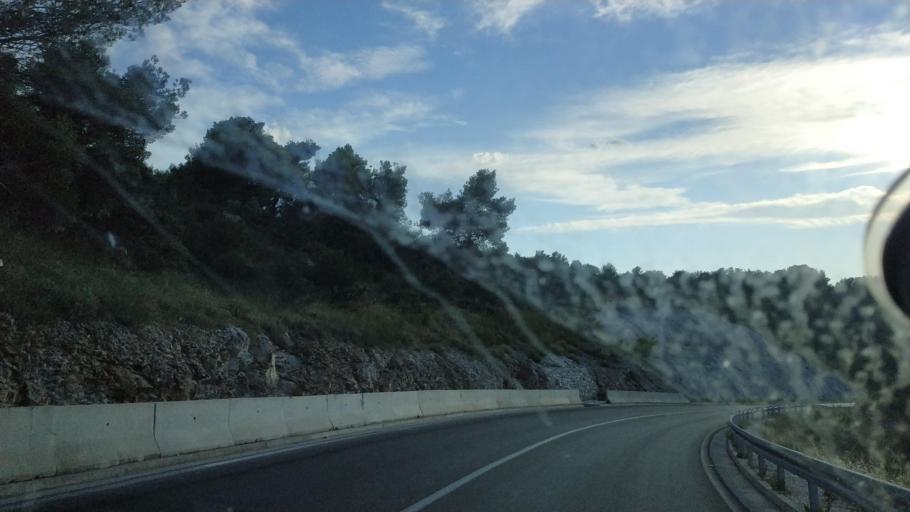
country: HR
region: Splitsko-Dalmatinska
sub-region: Grad Trogir
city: Trogir
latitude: 43.5087
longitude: 16.2761
